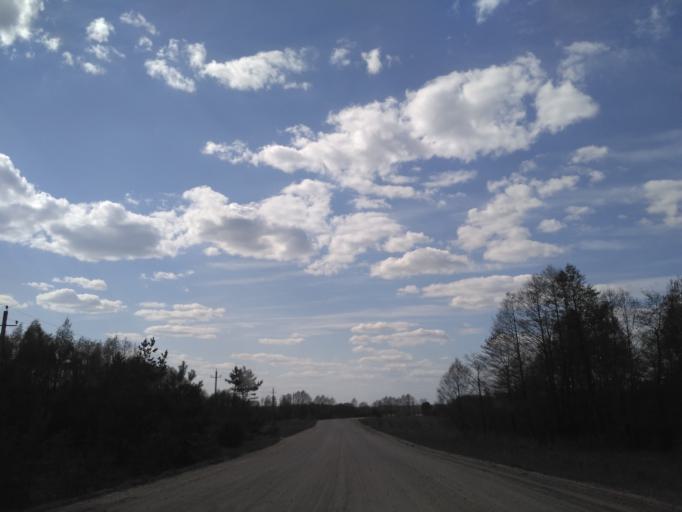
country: BY
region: Minsk
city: Narach
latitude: 54.9938
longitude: 26.5649
